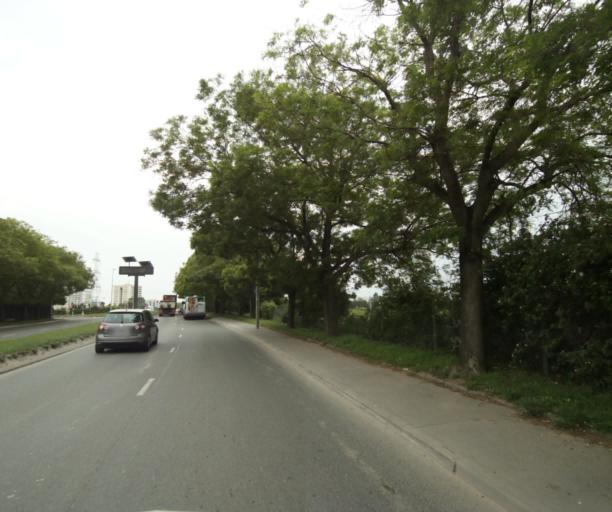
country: FR
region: Ile-de-France
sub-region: Departement des Hauts-de-Seine
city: Bois-Colombes
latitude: 48.9367
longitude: 2.2788
